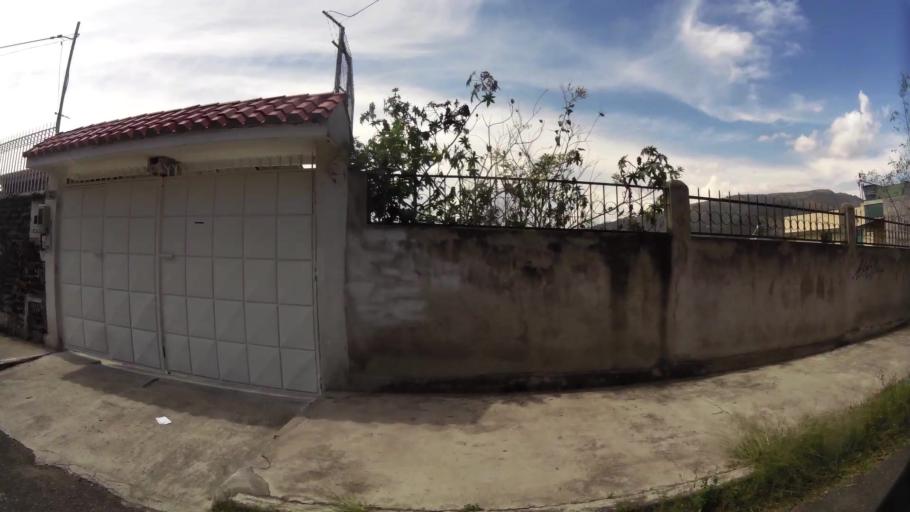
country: EC
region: Pichincha
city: Quito
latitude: -0.2147
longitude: -78.4325
